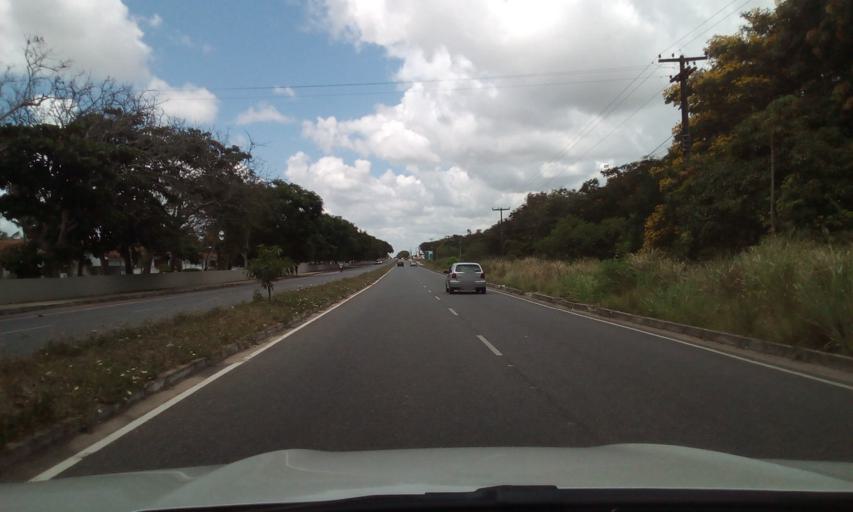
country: BR
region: Paraiba
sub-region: Bayeux
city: Bayeux
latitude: -7.1367
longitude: -34.9411
